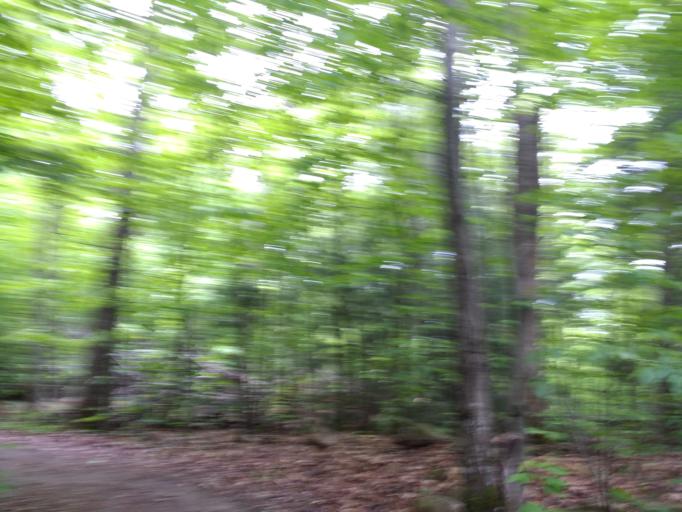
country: CA
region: Ontario
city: Huntsville
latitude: 45.5269
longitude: -78.7073
